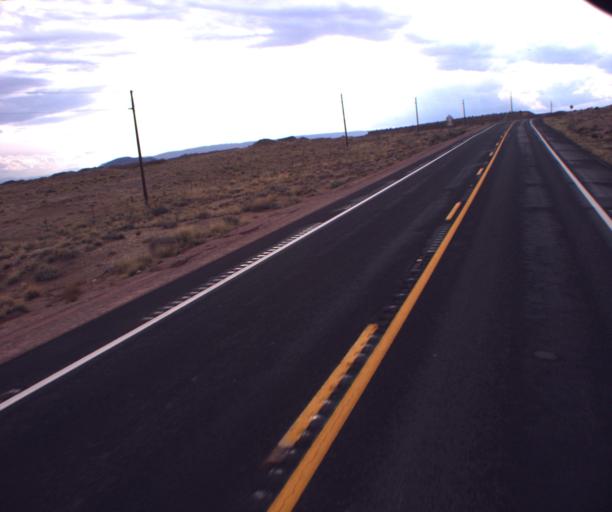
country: US
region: Arizona
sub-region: Coconino County
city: Tuba City
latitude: 36.0767
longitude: -111.3870
